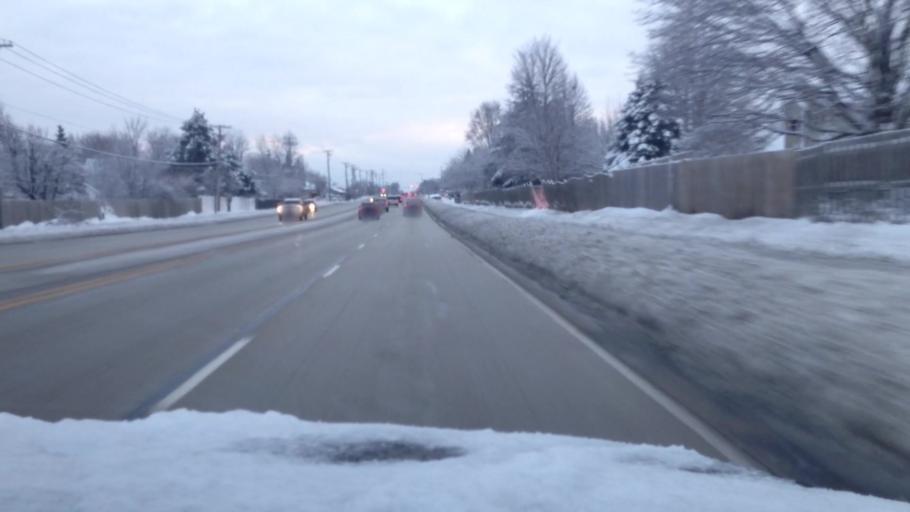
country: US
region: Illinois
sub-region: Kane County
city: South Elgin
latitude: 42.0020
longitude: -88.3157
